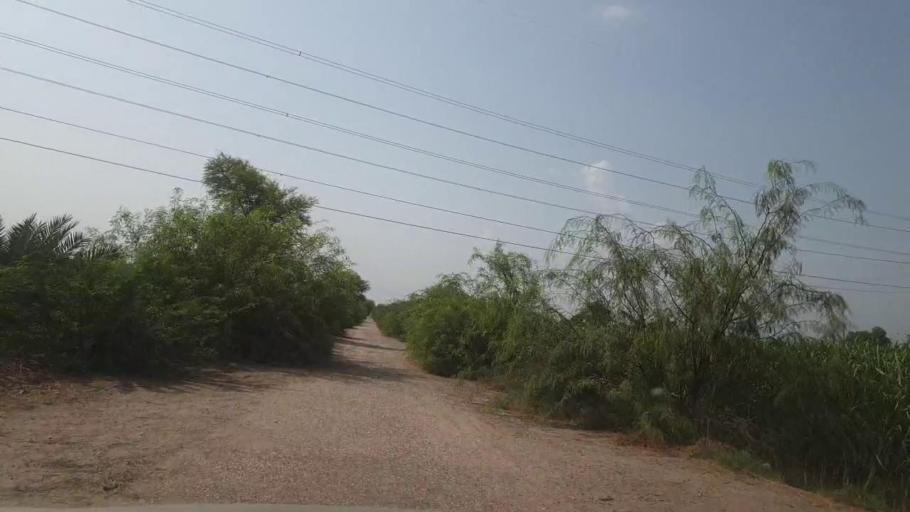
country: PK
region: Sindh
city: Pano Aqil
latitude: 27.7688
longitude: 69.1677
